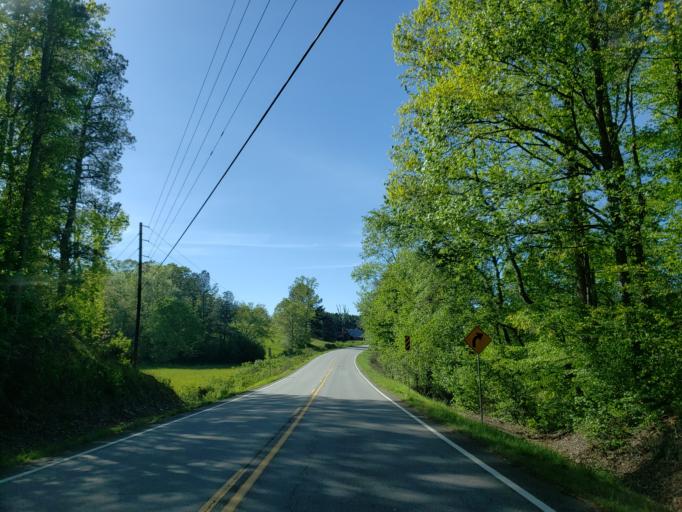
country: US
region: Georgia
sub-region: Haralson County
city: Tallapoosa
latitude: 33.8781
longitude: -85.3075
